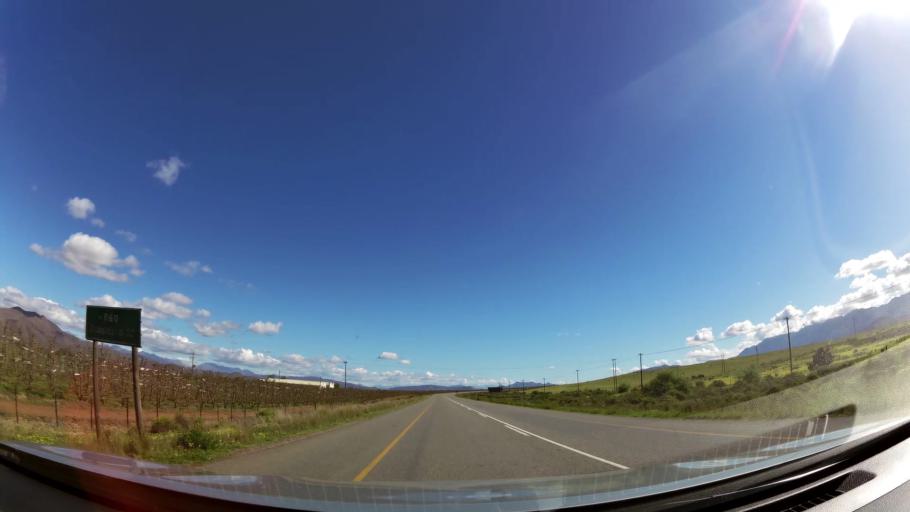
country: ZA
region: Western Cape
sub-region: Cape Winelands District Municipality
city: Ashton
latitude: -33.8393
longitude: 20.0149
